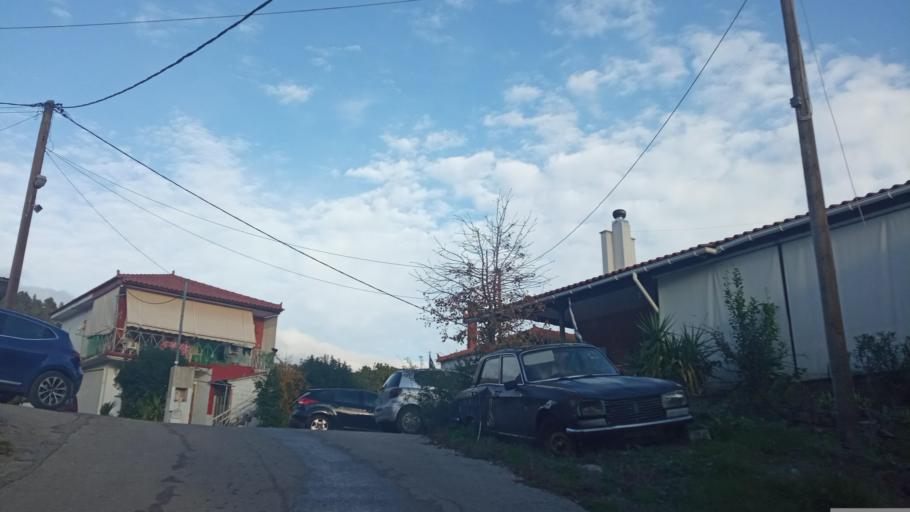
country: GR
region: Central Greece
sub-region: Nomos Evvoias
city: Psachna
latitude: 38.6198
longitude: 23.7353
